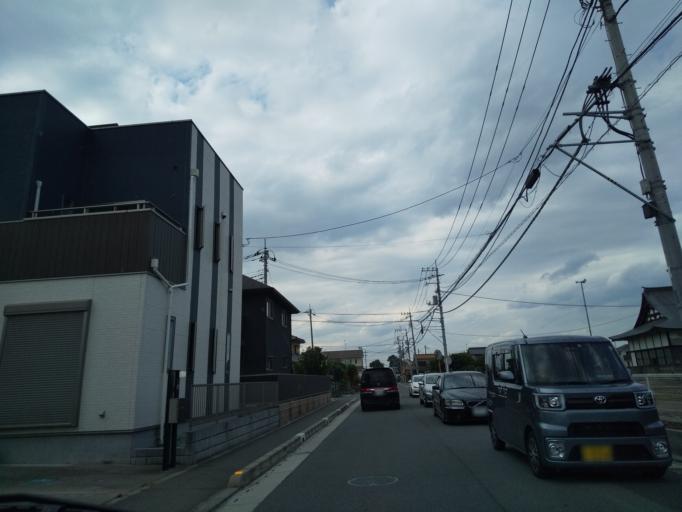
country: JP
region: Chiba
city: Noda
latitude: 35.9888
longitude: 139.8130
